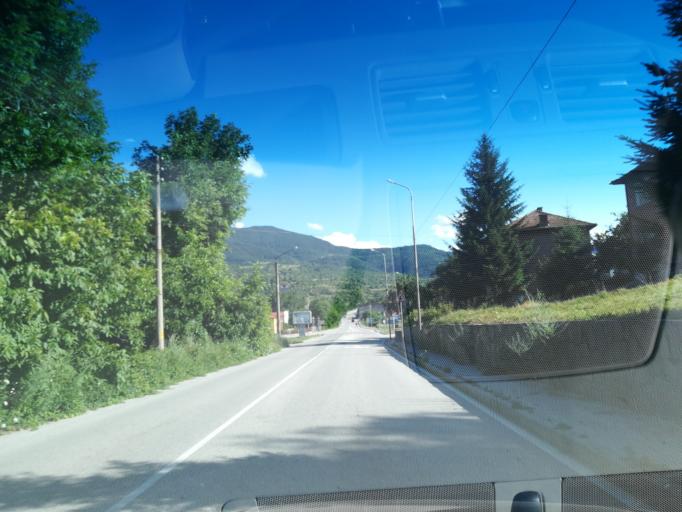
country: BG
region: Plovdiv
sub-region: Obshtina Luki
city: Luki
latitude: 41.8719
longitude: 24.6910
